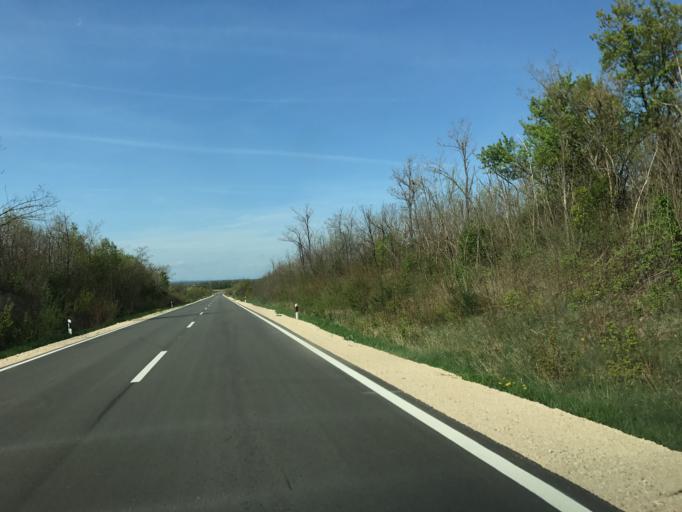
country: RS
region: Central Serbia
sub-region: Borski Okrug
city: Negotin
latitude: 44.1791
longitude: 22.3653
